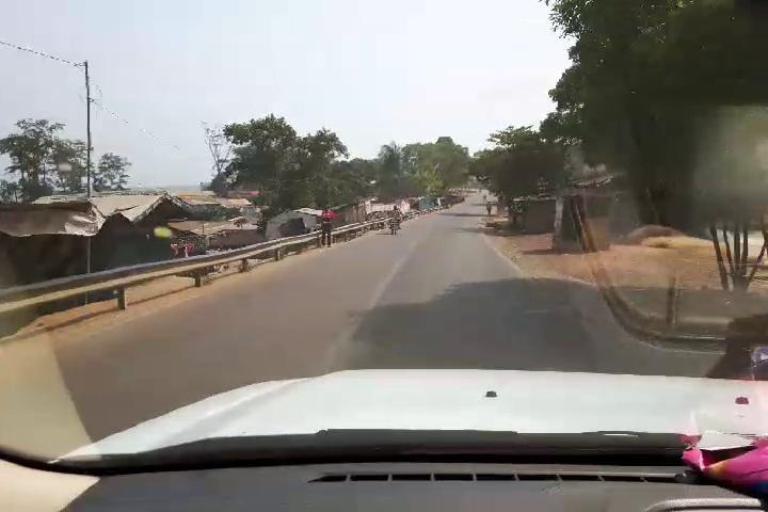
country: SL
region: Western Area
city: Waterloo
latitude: 8.2104
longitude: -13.1030
